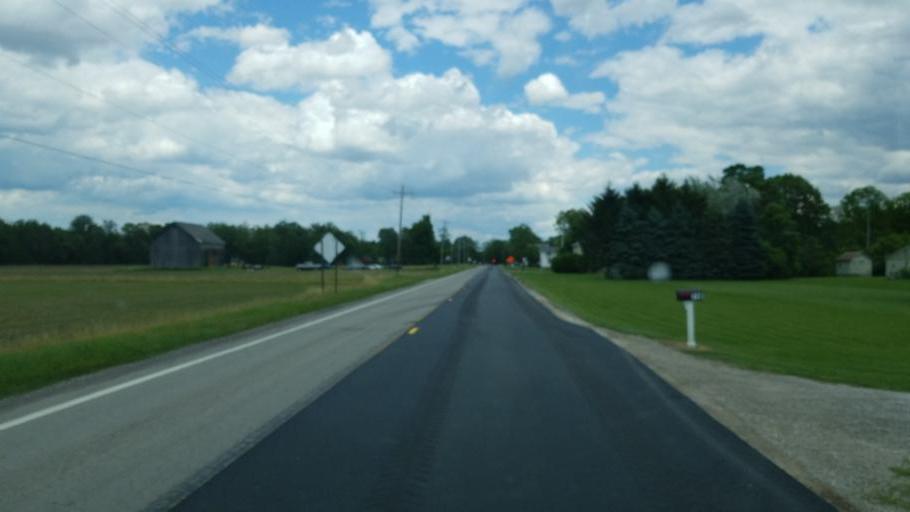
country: US
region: Ohio
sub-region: Erie County
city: Milan
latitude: 41.3011
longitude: -82.6196
